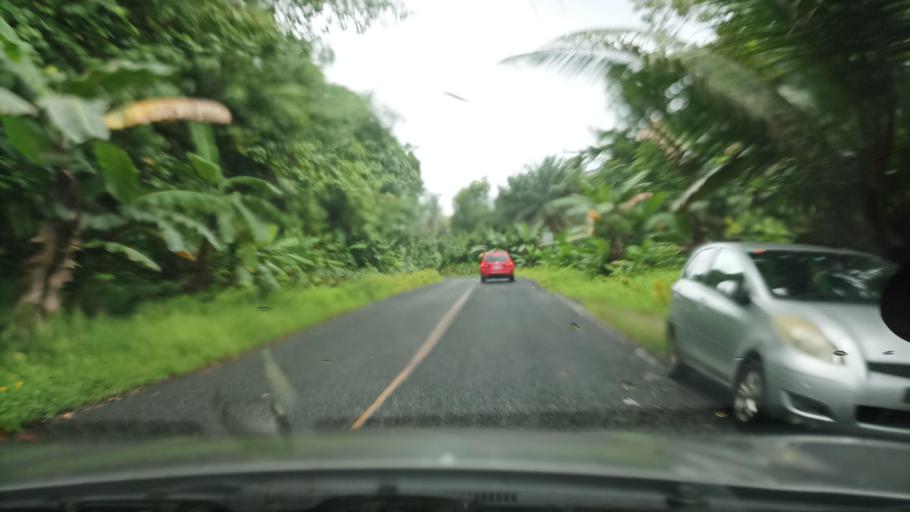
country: FM
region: Pohnpei
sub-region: Madolenihm Municipality
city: Madolenihm Municipality Government
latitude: 6.8089
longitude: 158.2569
